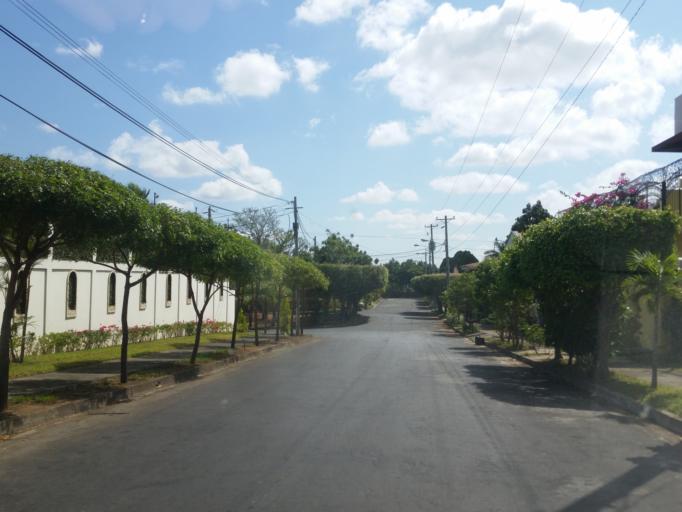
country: NI
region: Managua
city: Managua
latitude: 12.0984
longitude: -86.2573
